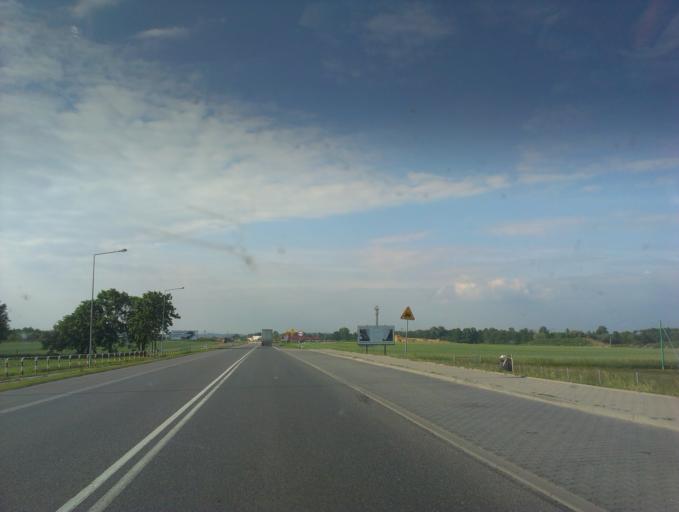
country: PL
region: Lower Silesian Voivodeship
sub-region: Powiat trzebnicki
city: Psary
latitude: 51.2103
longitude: 17.0402
